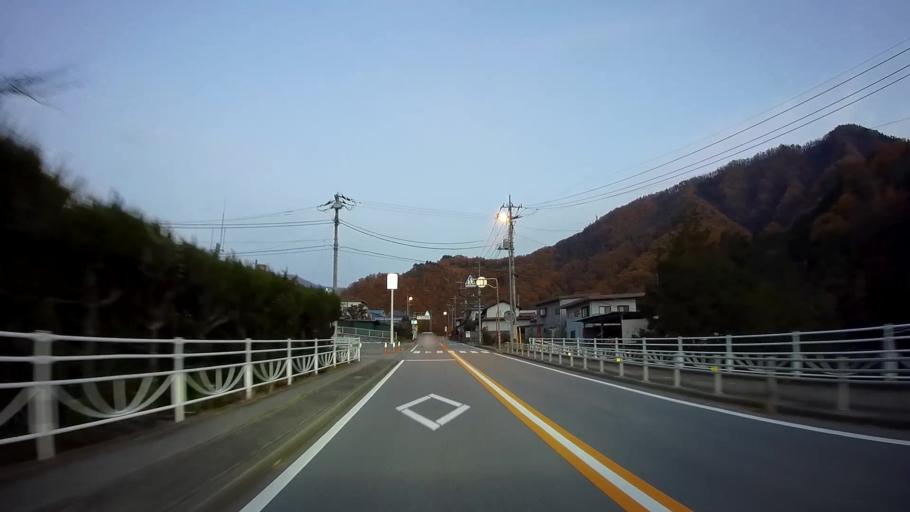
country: JP
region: Yamanashi
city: Enzan
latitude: 35.6391
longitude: 138.7792
